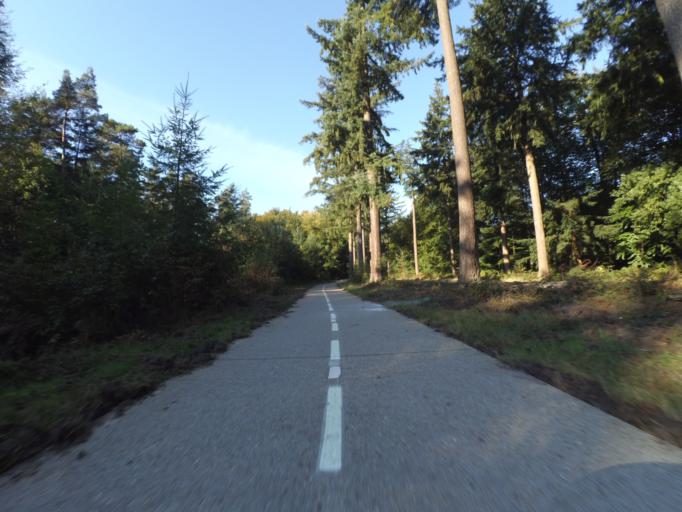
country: NL
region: Gelderland
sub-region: Gemeente Barneveld
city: Garderen
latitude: 52.2657
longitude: 5.6885
